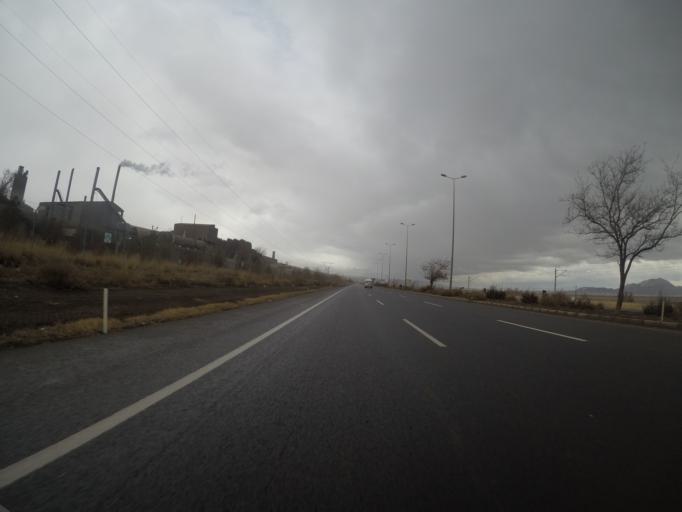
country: TR
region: Kayseri
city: Incesu
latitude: 38.7102
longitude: 35.2619
